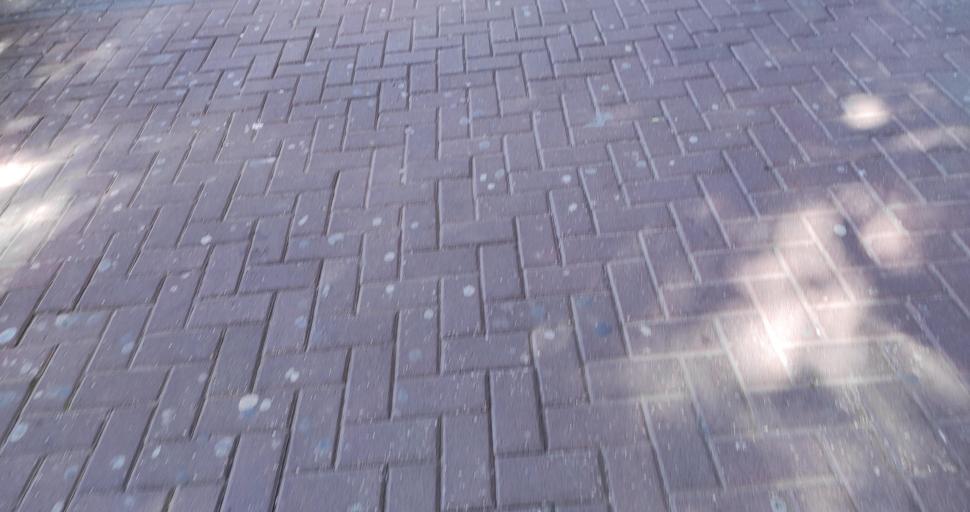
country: IL
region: Central District
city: Netanya
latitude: 32.3264
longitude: 34.8575
